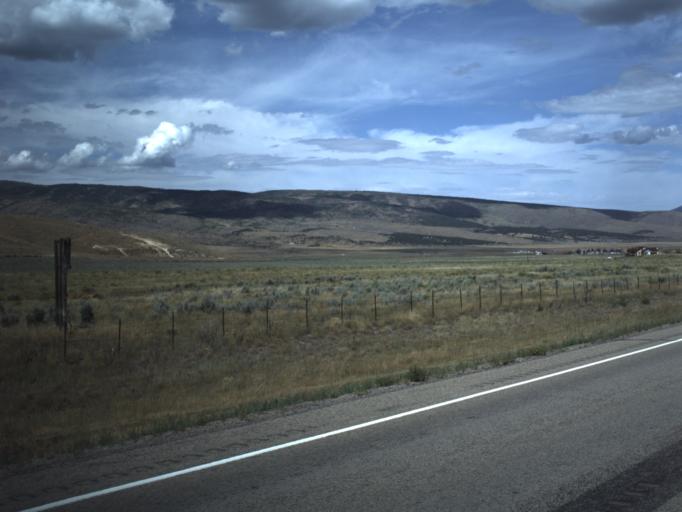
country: US
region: Utah
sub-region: Sanpete County
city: Fairview
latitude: 39.7544
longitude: -111.4801
